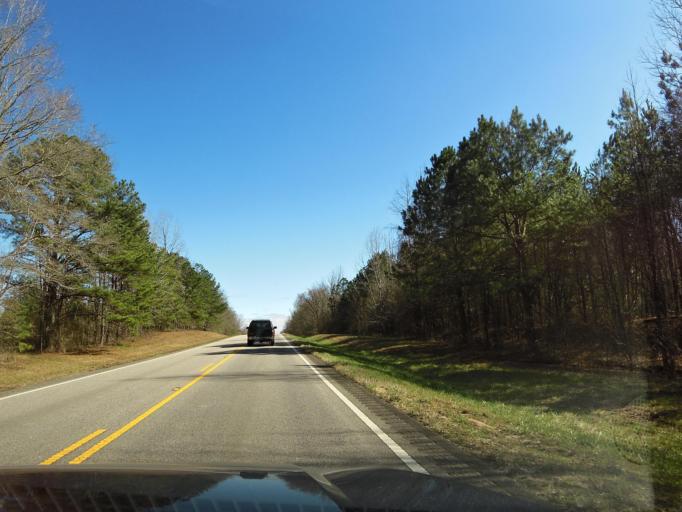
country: US
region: Alabama
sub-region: Barbour County
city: Clayton
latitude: 32.0651
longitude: -85.4730
